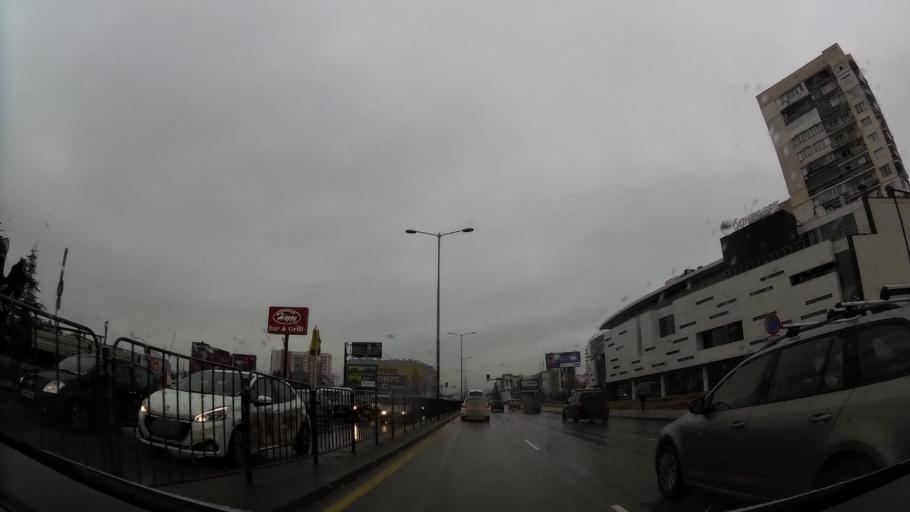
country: BG
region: Sofia-Capital
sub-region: Stolichna Obshtina
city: Sofia
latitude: 42.6490
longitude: 23.3775
